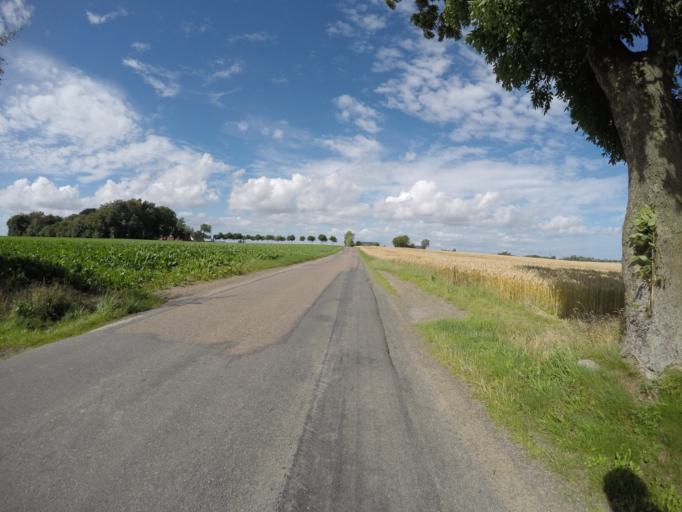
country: SE
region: Skane
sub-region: Simrishamns Kommun
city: Simrishamn
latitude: 55.4886
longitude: 14.1948
